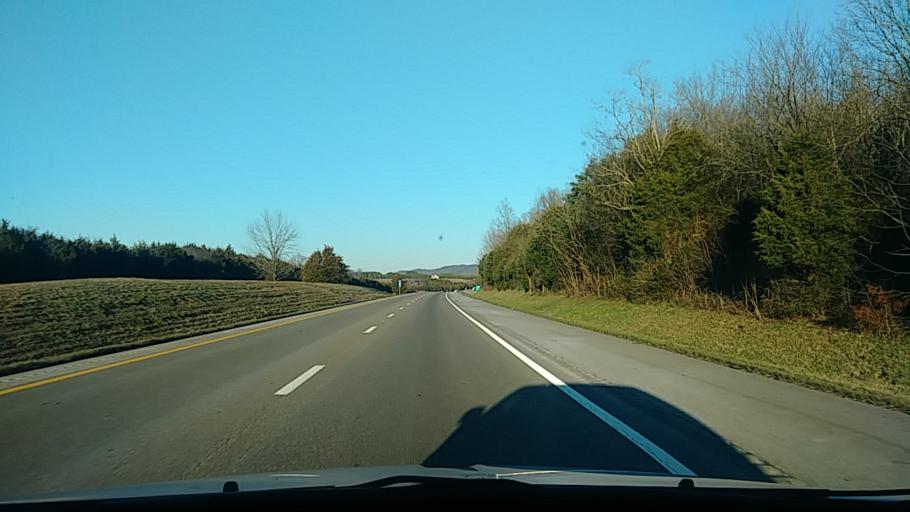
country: US
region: Tennessee
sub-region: Hamblen County
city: Morristown
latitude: 36.1898
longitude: -83.1825
